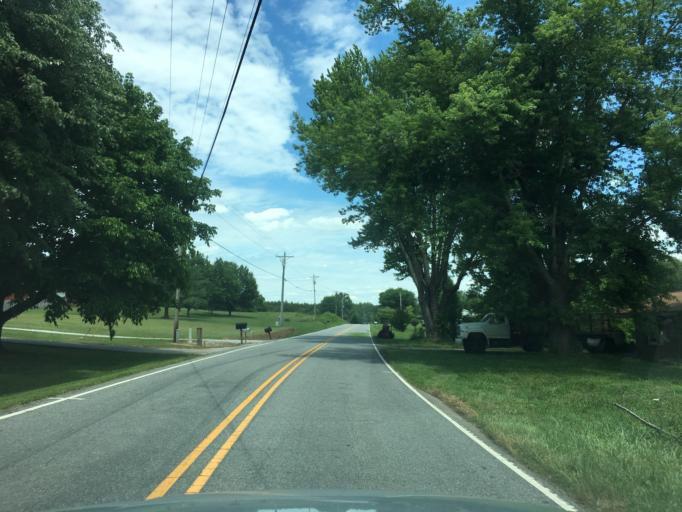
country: US
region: North Carolina
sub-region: Burke County
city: Glen Alpine
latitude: 35.6787
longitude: -81.7690
